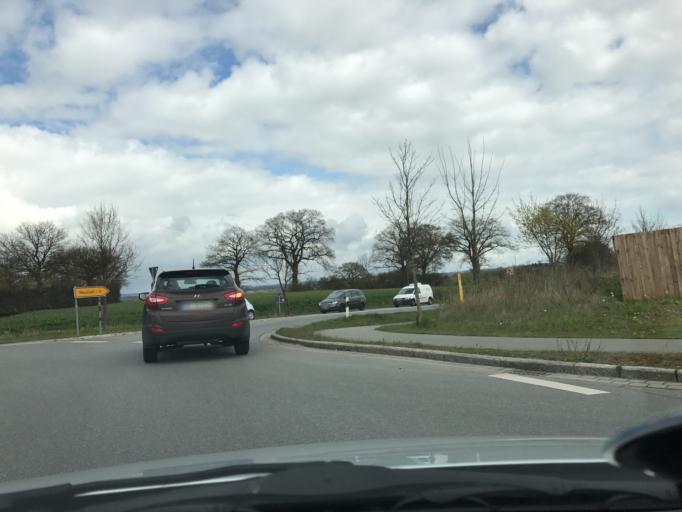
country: DE
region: Schleswig-Holstein
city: Neustadt in Holstein
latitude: 54.0955
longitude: 10.7850
